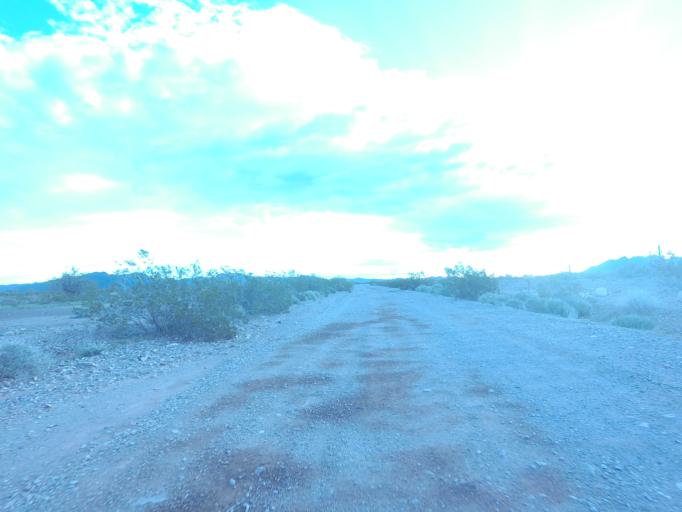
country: US
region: Arizona
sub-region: La Paz County
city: Quartzsite
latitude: 33.5331
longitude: -114.1939
